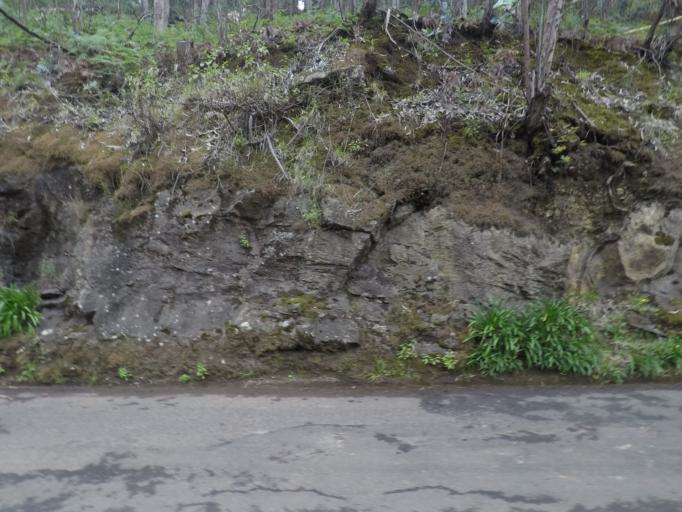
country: PT
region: Madeira
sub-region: Calheta
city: Estreito da Calheta
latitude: 32.7536
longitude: -17.1940
